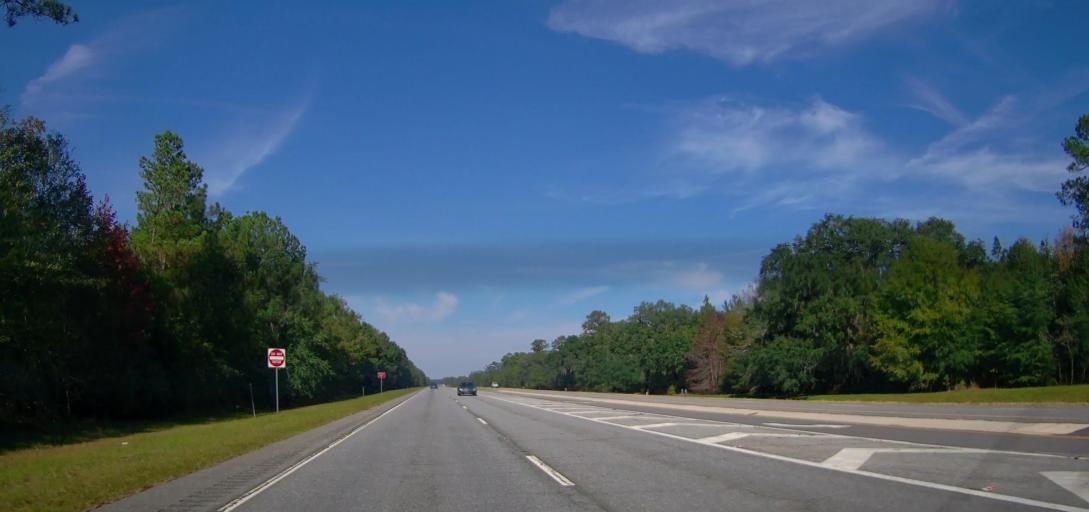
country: US
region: Georgia
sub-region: Lee County
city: Leesburg
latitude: 31.7071
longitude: -83.9904
